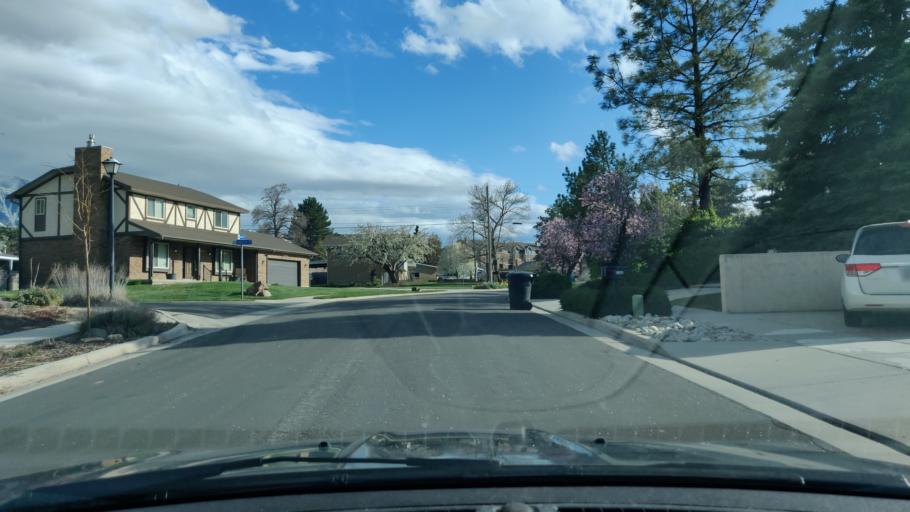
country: US
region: Utah
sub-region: Salt Lake County
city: Little Cottonwood Creek Valley
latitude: 40.6174
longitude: -111.8327
